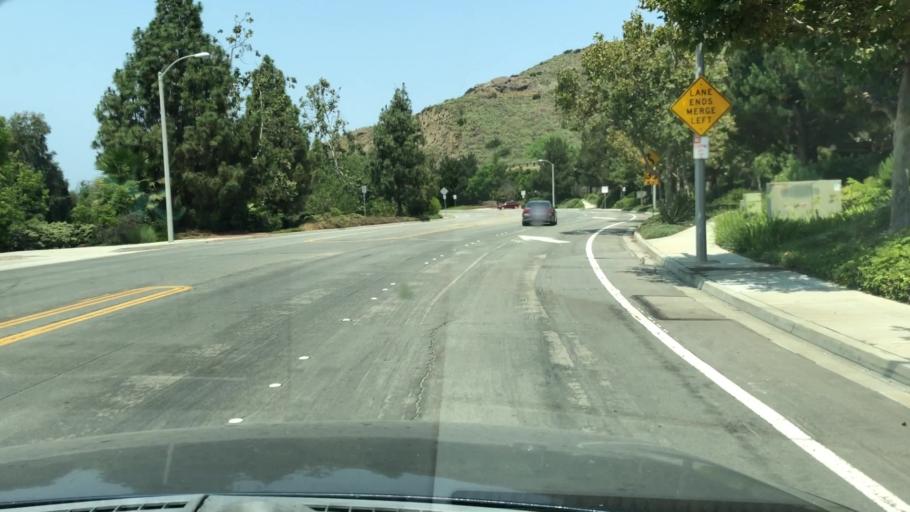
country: US
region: California
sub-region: Ventura County
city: Casa Conejo
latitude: 34.2035
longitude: -118.9863
